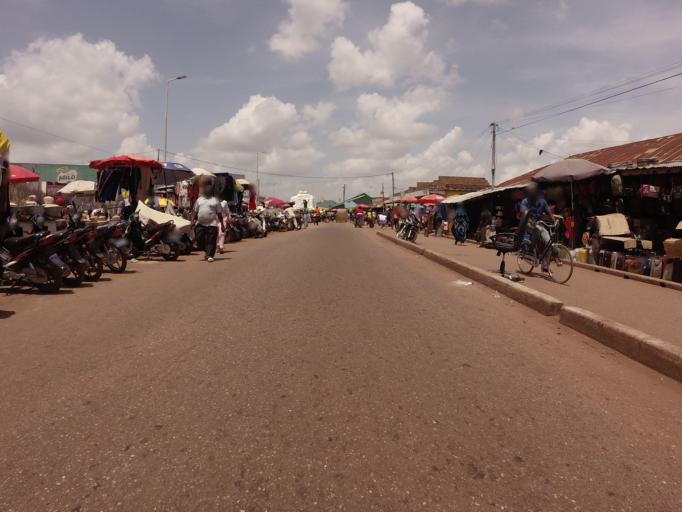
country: GH
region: Northern
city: Tamale
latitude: 9.4037
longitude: -0.8432
